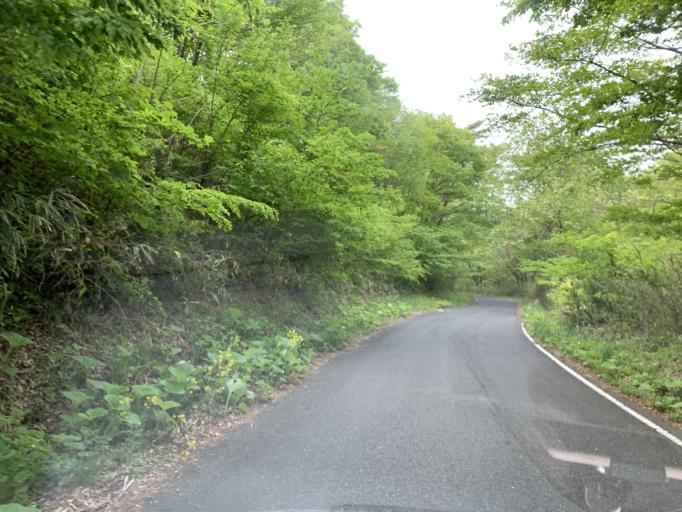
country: JP
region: Iwate
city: Ichinoseki
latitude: 38.8676
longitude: 141.0655
